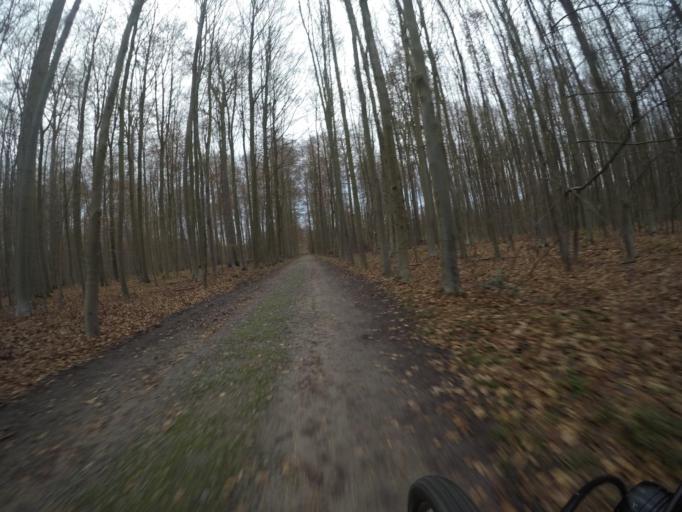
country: BE
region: Flanders
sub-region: Provincie Vlaams-Brabant
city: Hoeilaart
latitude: 50.7544
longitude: 4.4465
